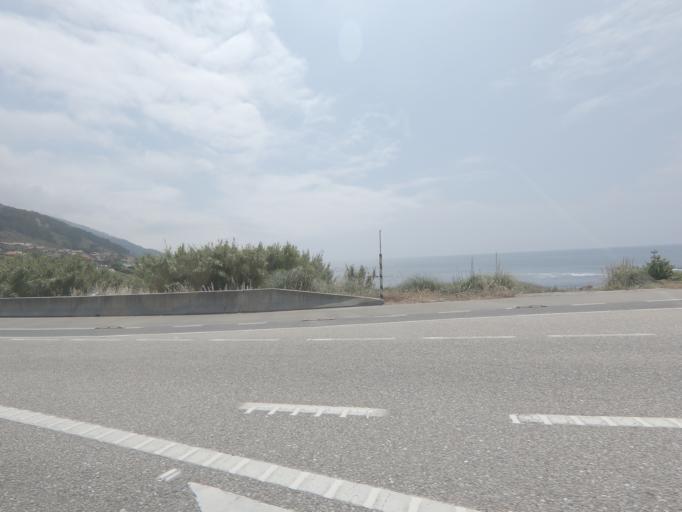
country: ES
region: Galicia
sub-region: Provincia de Pontevedra
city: Baiona
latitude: 42.1009
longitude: -8.8947
